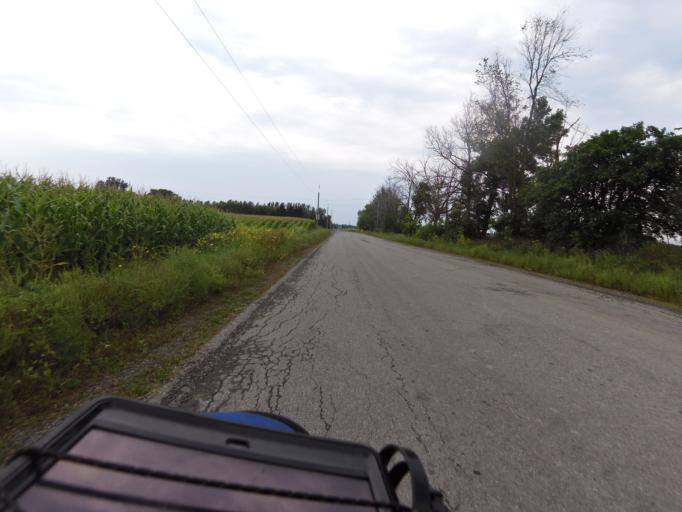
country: CA
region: Ontario
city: Casselman
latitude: 45.1750
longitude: -75.4117
